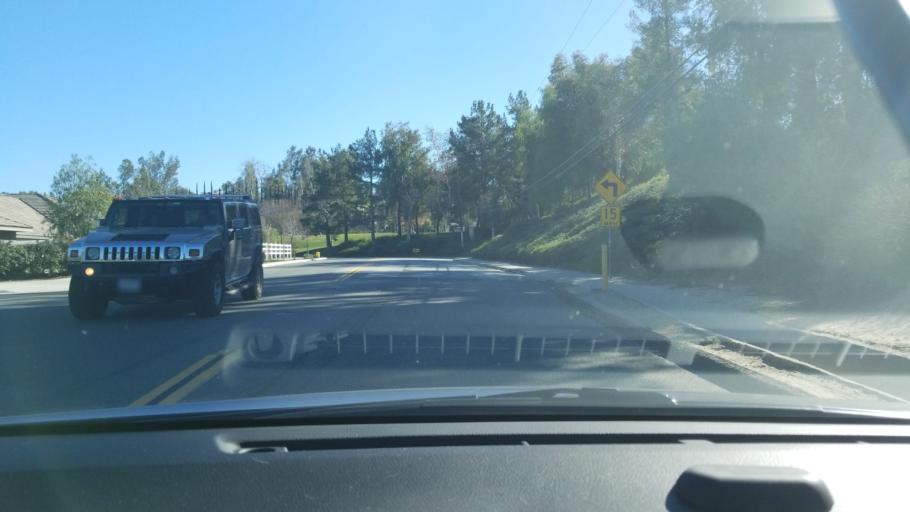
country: US
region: California
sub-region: Riverside County
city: Murrieta Hot Springs
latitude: 33.5411
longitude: -117.1107
